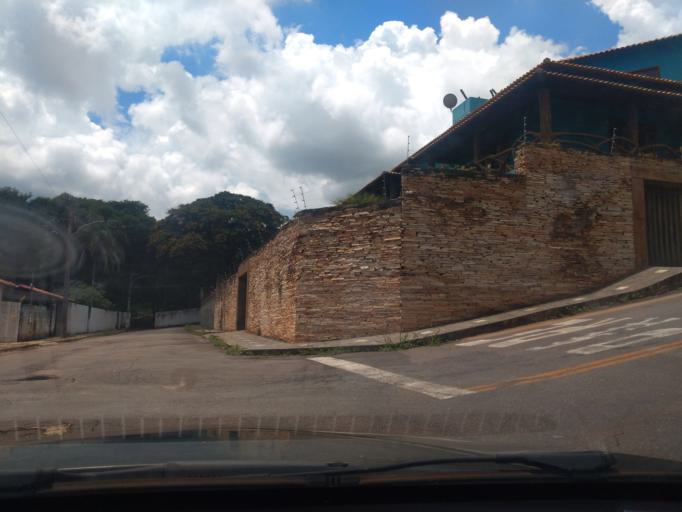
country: BR
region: Minas Gerais
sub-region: Tres Coracoes
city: Tres Coracoes
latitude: -21.6955
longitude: -45.2646
